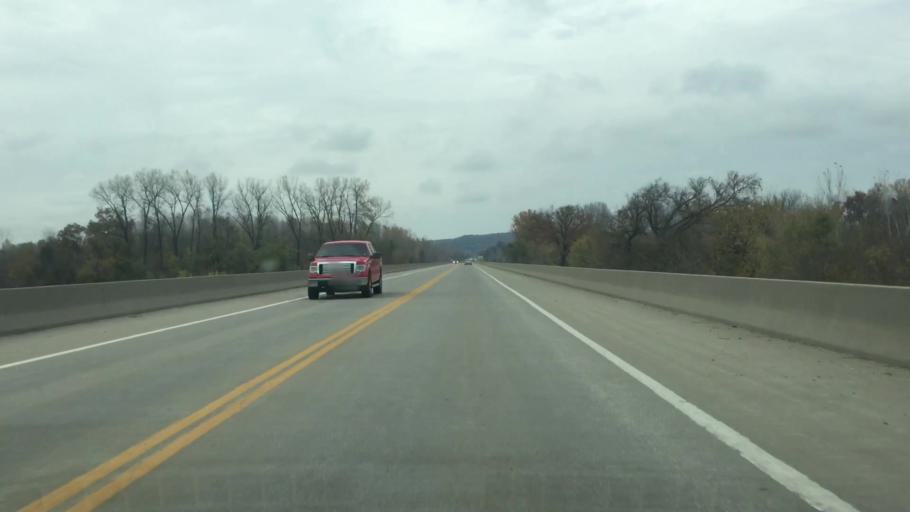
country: US
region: Missouri
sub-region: Gasconade County
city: Hermann
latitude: 38.7161
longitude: -91.4413
